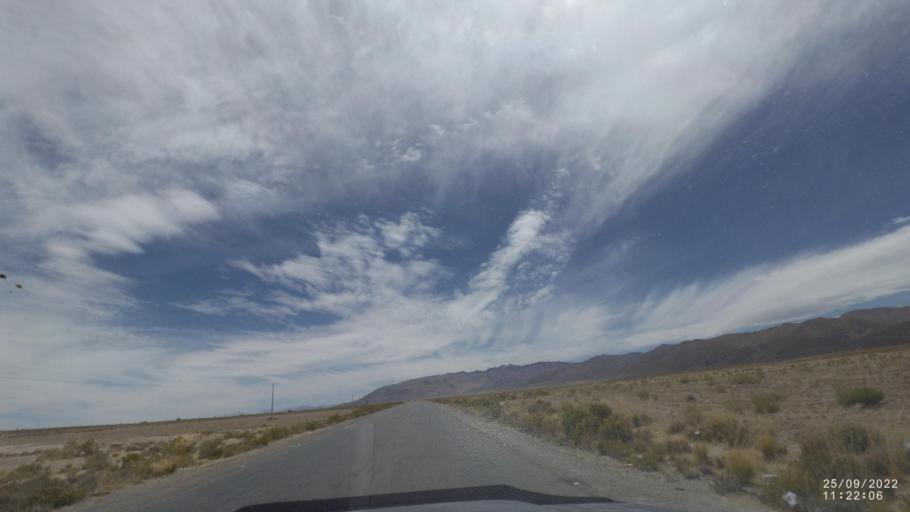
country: BO
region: Oruro
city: Challapata
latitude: -19.1316
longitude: -66.7687
